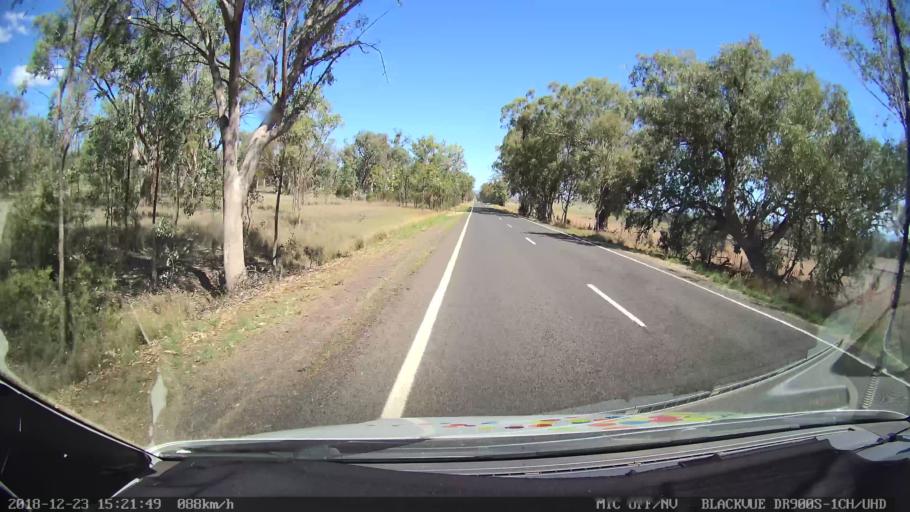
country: AU
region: New South Wales
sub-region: Tamworth Municipality
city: Manilla
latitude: -30.8612
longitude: 150.7995
